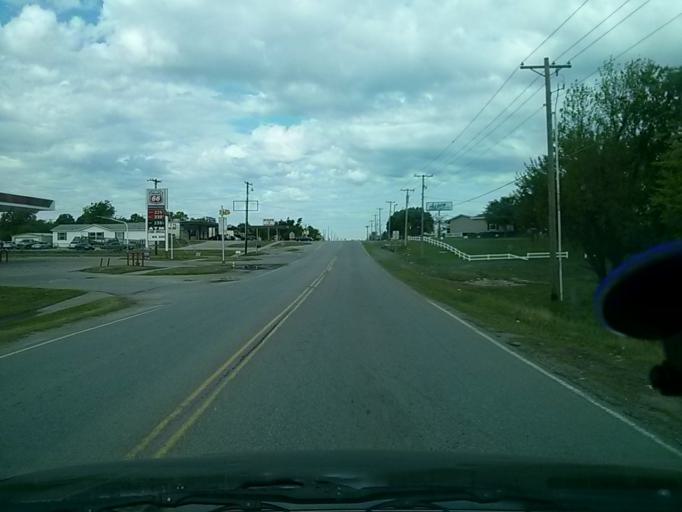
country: US
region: Oklahoma
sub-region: Rogers County
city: Catoosa
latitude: 36.1607
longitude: -95.8438
